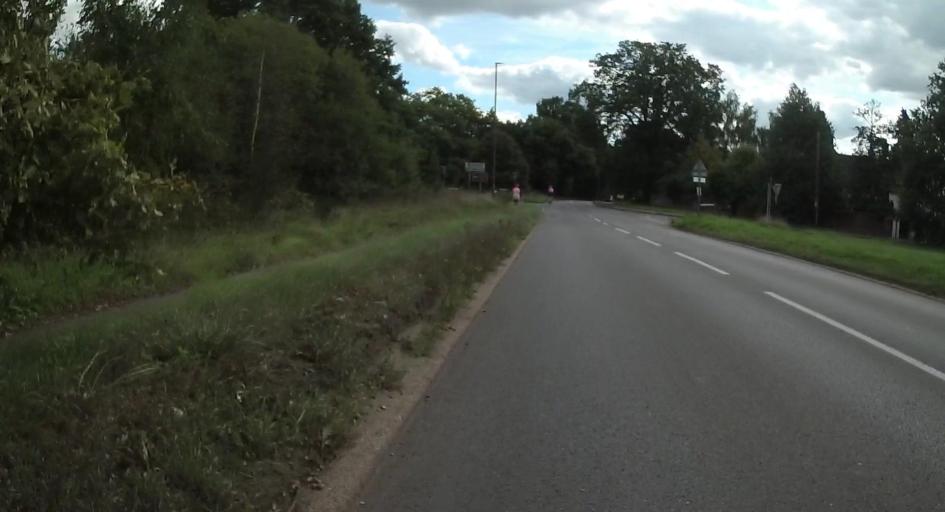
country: GB
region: England
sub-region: Surrey
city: Chobham
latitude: 51.3568
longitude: -0.6071
